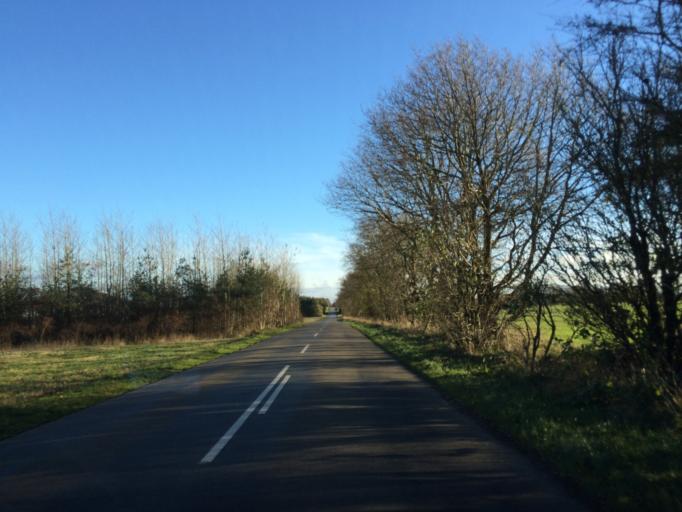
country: DK
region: Central Jutland
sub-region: Herning Kommune
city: Kibaek
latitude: 56.0597
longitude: 8.7717
